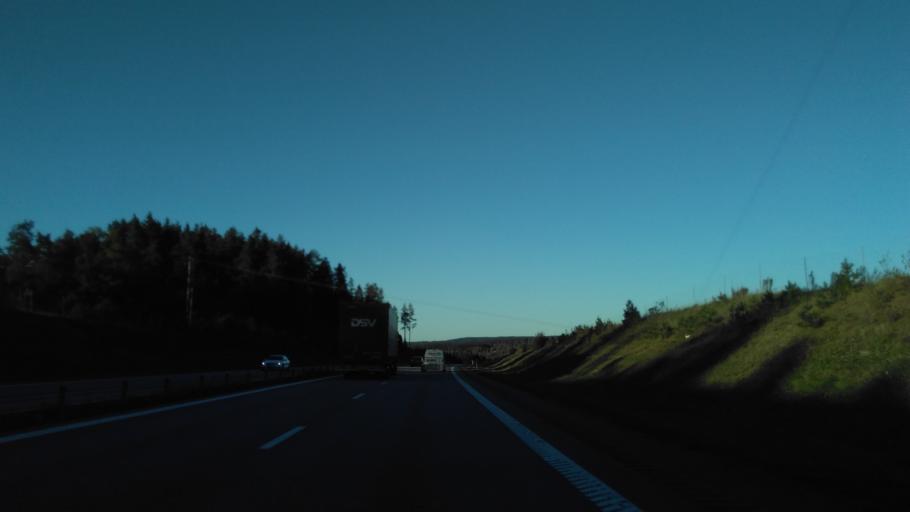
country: SE
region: Vaestra Goetaland
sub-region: Boras Kommun
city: Dalsjofors
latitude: 57.7787
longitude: 13.1180
